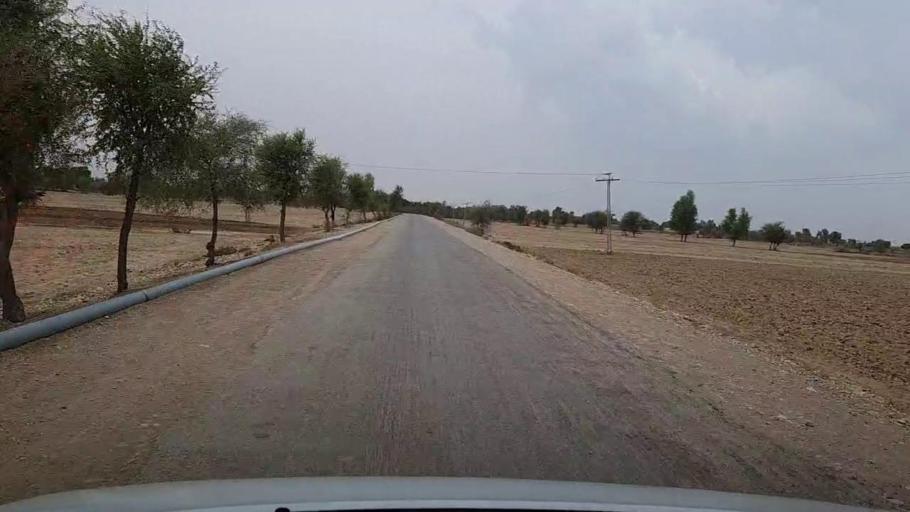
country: PK
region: Sindh
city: Sehwan
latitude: 26.3202
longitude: 67.7330
